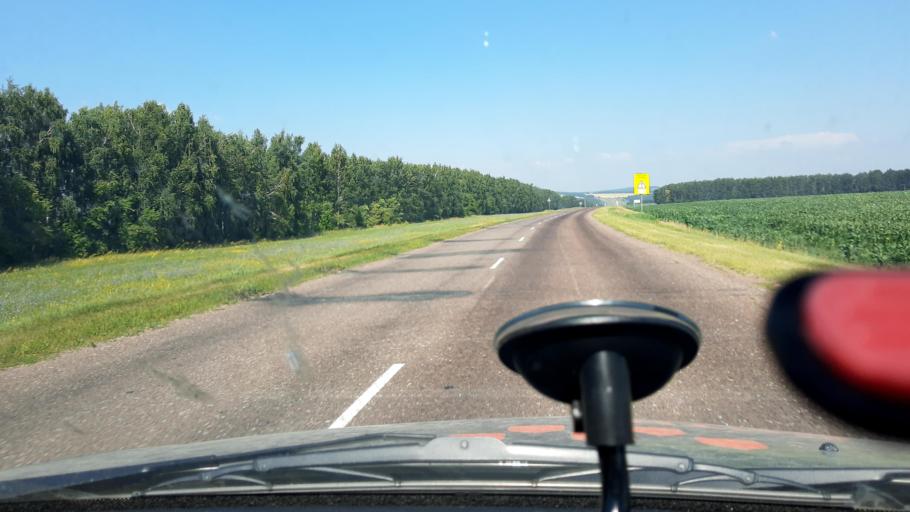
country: RU
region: Bashkortostan
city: Chekmagush
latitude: 55.1127
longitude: 54.6556
